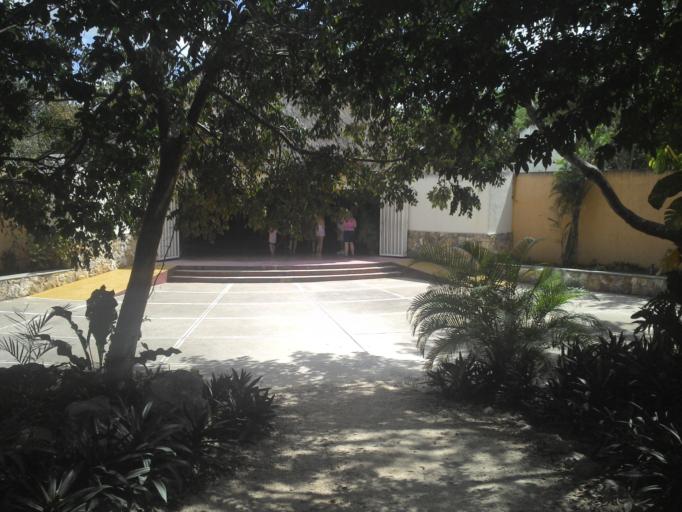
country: MX
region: Yucatan
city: Temozon
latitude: 20.8883
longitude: -88.1355
